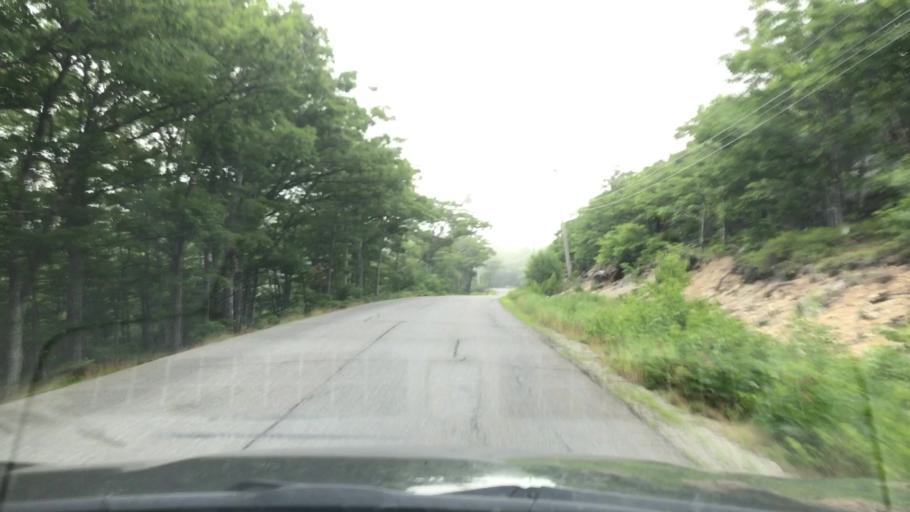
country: US
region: Maine
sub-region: Hancock County
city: Bar Harbor
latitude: 44.3532
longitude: -68.1841
